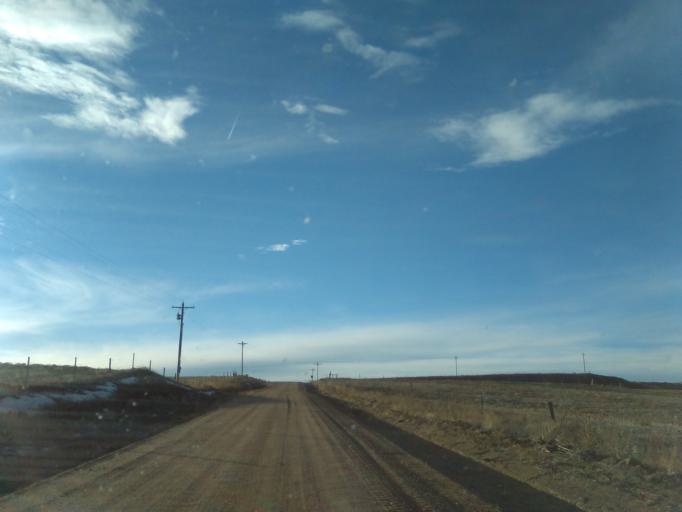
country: US
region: Nebraska
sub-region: Morrill County
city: Bridgeport
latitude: 41.4820
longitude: -102.9809
